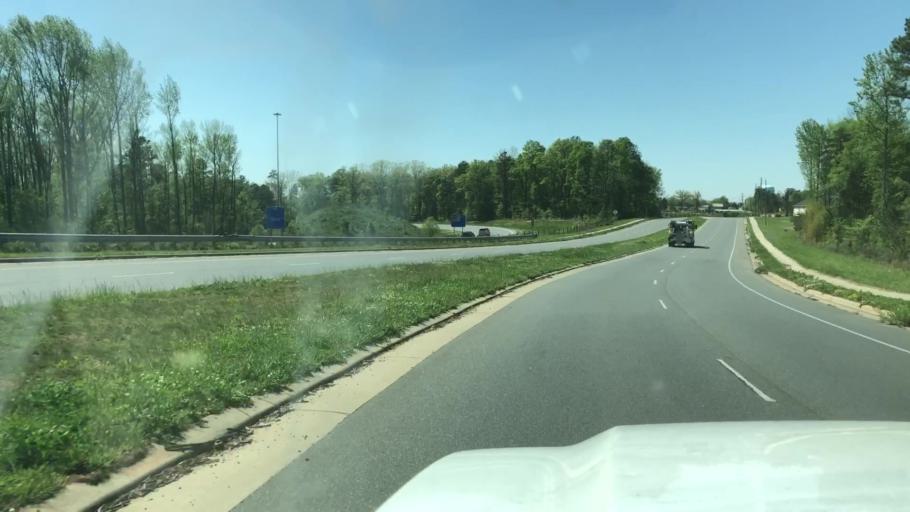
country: US
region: North Carolina
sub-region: Mecklenburg County
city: Huntersville
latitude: 35.3672
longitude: -80.8231
